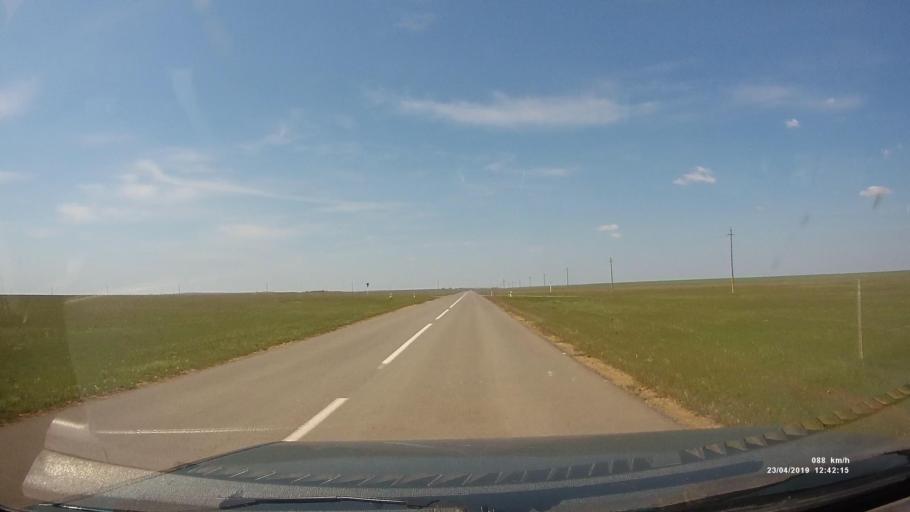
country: RU
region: Kalmykiya
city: Yashalta
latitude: 46.4545
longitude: 42.6685
